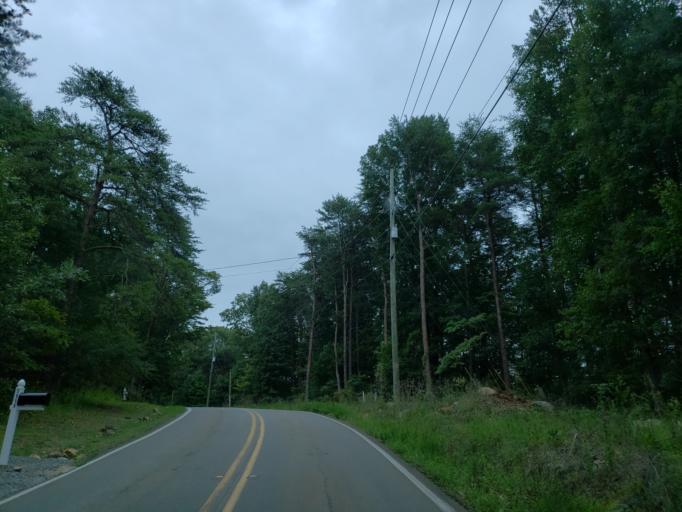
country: US
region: Georgia
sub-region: Pickens County
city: Jasper
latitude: 34.4198
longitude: -84.5397
